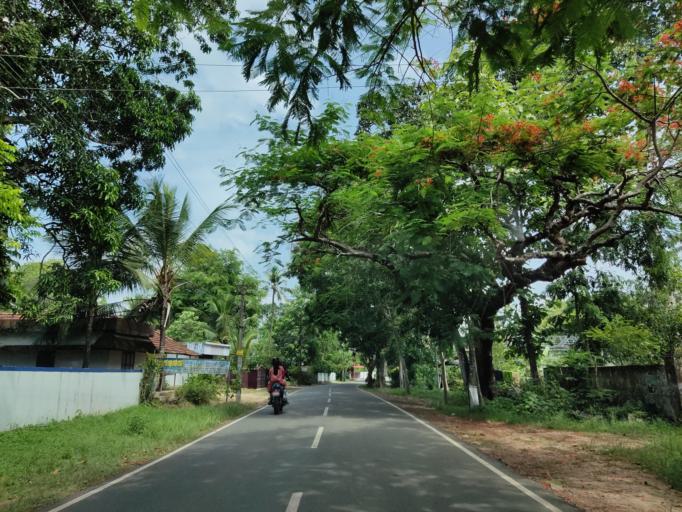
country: IN
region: Kerala
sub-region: Alappuzha
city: Mavelikara
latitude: 9.2726
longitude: 76.5659
